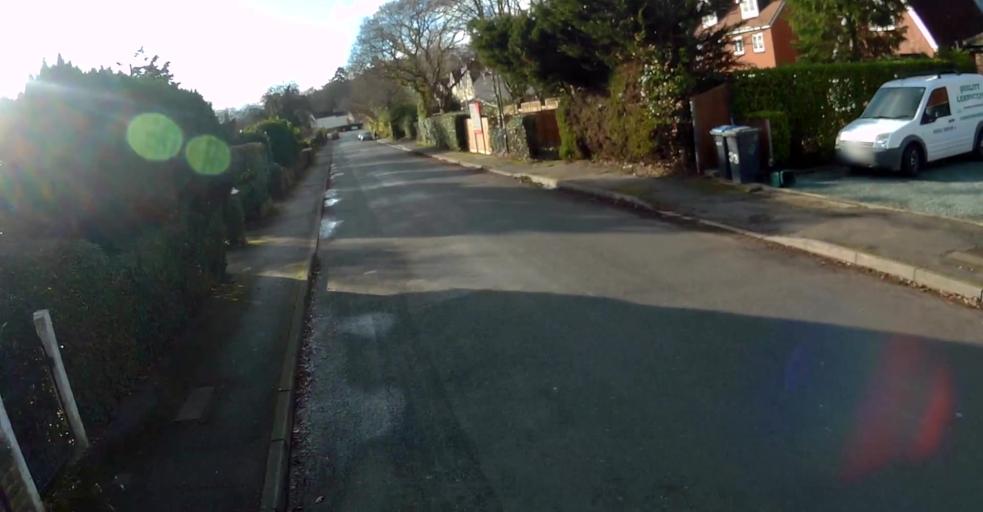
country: GB
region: England
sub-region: Surrey
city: Ottershaw
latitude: 51.3636
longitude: -0.5251
